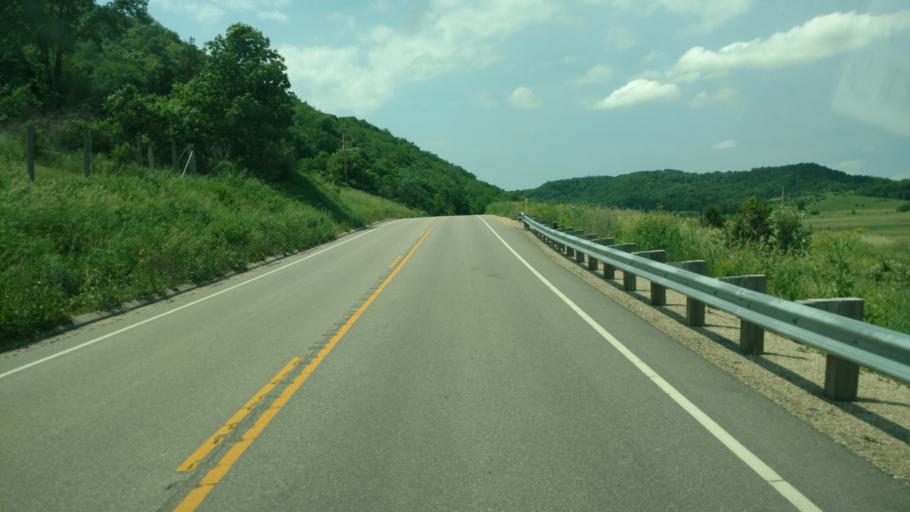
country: US
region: Wisconsin
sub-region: Vernon County
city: Viroqua
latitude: 43.5171
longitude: -90.6632
